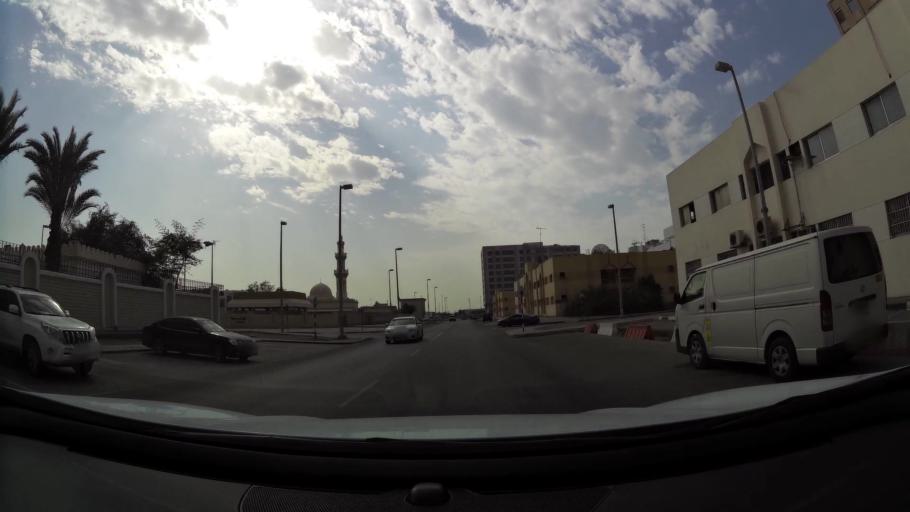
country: AE
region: Abu Dhabi
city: Abu Dhabi
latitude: 24.3217
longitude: 54.5330
